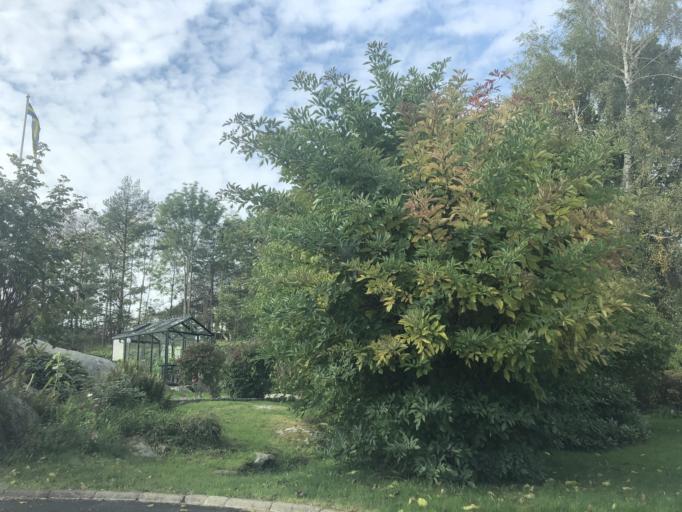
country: SE
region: Vaestra Goetaland
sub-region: Goteborg
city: Majorna
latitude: 57.6575
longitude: 11.8683
